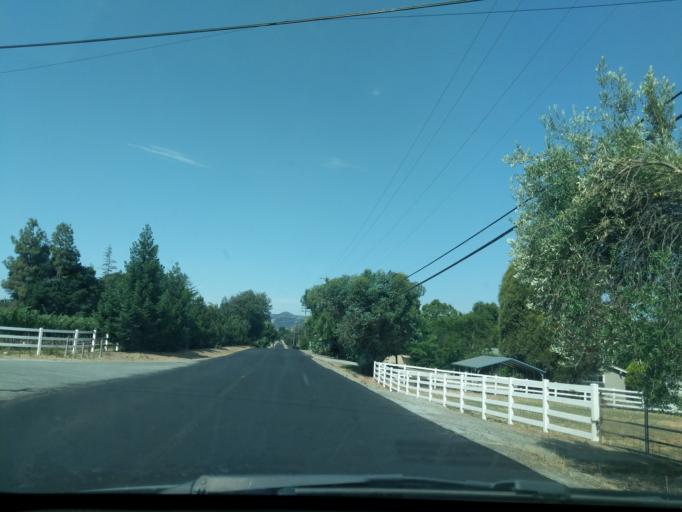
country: US
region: California
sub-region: Santa Clara County
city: San Martin
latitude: 37.0798
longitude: -121.5663
